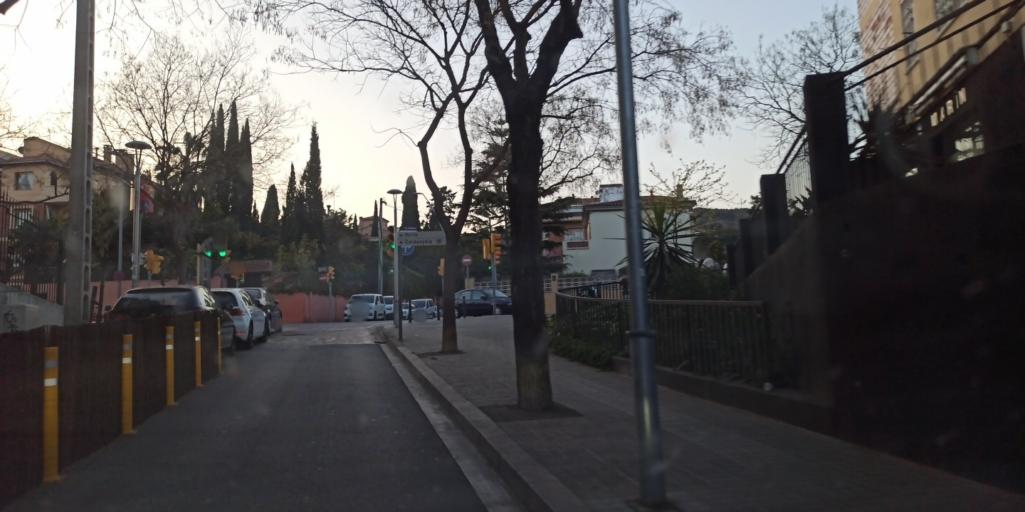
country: ES
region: Catalonia
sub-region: Provincia de Barcelona
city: Nou Barris
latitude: 41.4375
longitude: 2.1569
